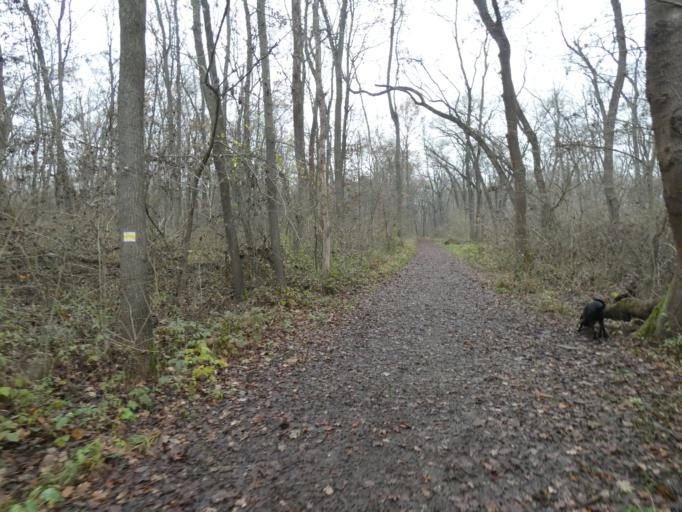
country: HU
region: Pest
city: Ocsa
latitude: 47.2643
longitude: 19.2314
